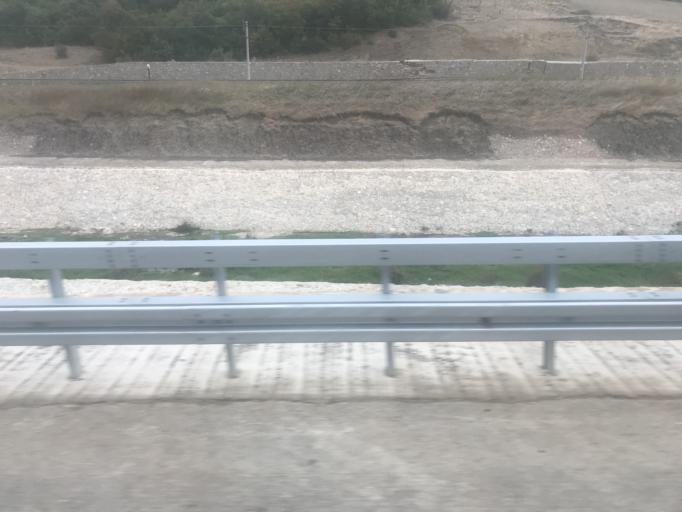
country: TR
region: Balikesir
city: Omerkoy
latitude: 39.8709
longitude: 28.0915
